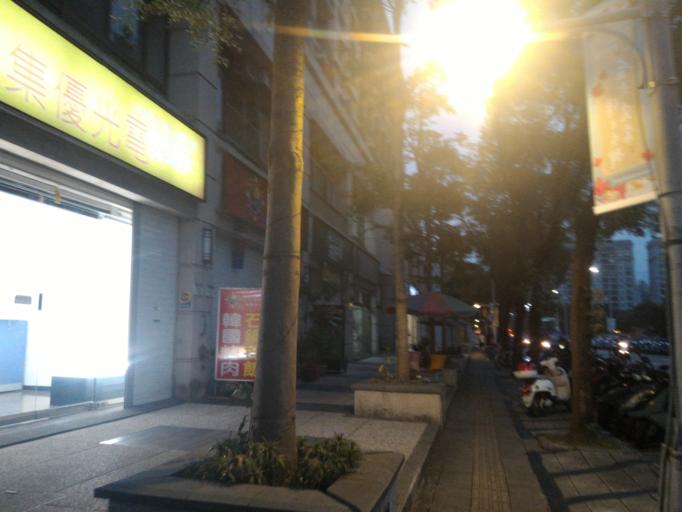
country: TW
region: Taiwan
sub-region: Taoyuan
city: Taoyuan
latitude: 24.9467
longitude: 121.3725
